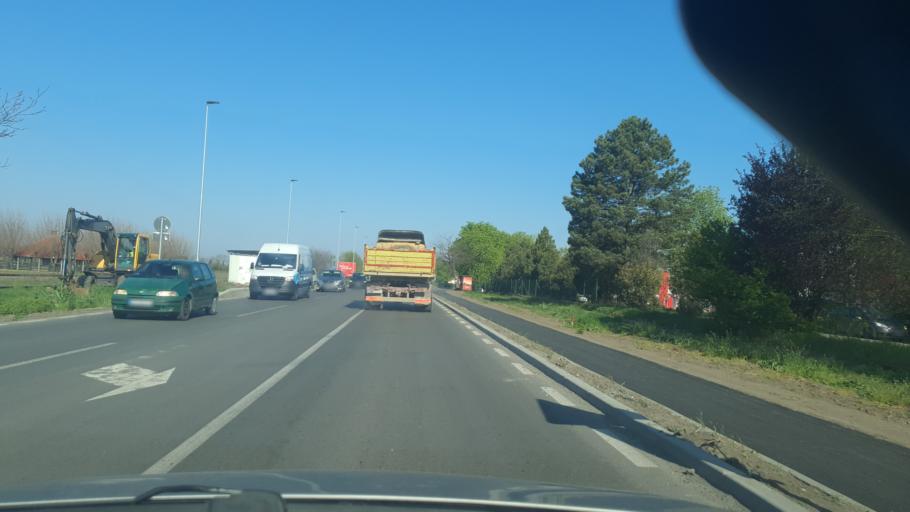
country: RS
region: Autonomna Pokrajina Vojvodina
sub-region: Juznobacki Okrug
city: Vrbas
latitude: 45.5849
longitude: 19.6102
